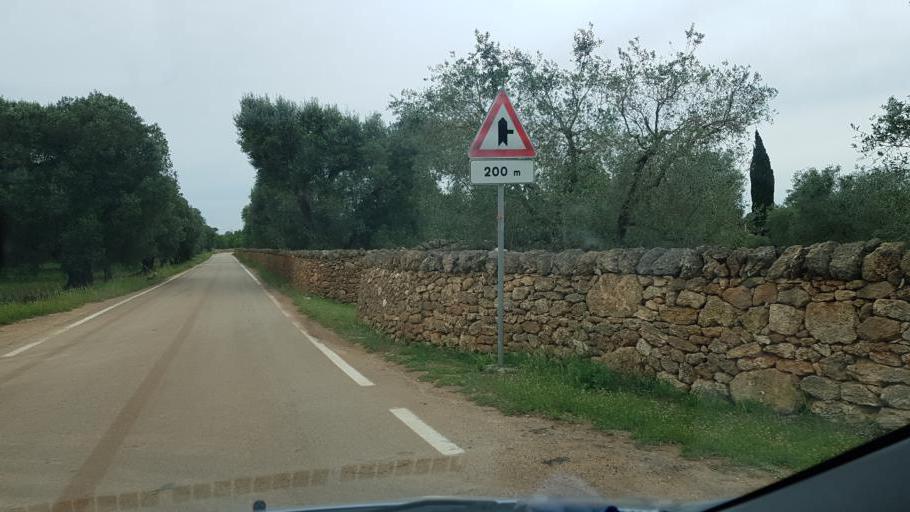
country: IT
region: Apulia
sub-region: Provincia di Brindisi
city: San Vito dei Normanni
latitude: 40.6689
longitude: 17.7558
